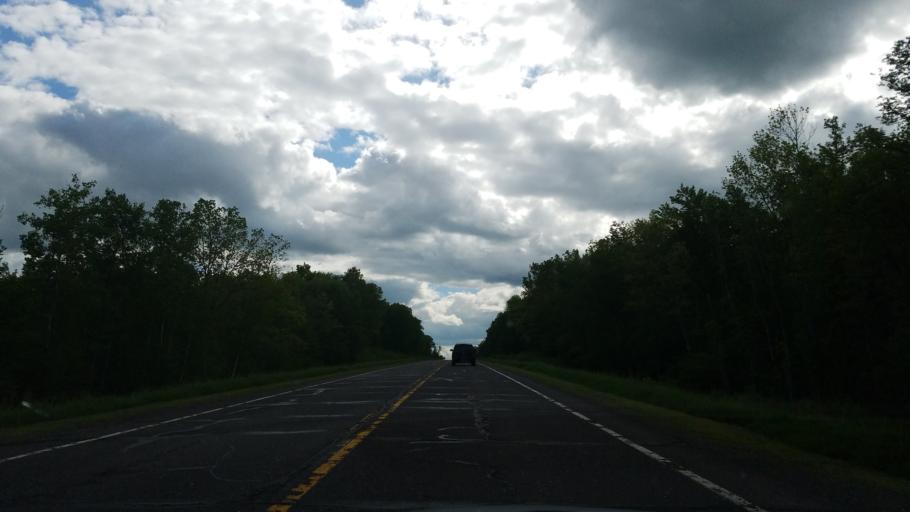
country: US
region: Wisconsin
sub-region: Burnett County
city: Siren
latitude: 46.1733
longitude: -92.2213
